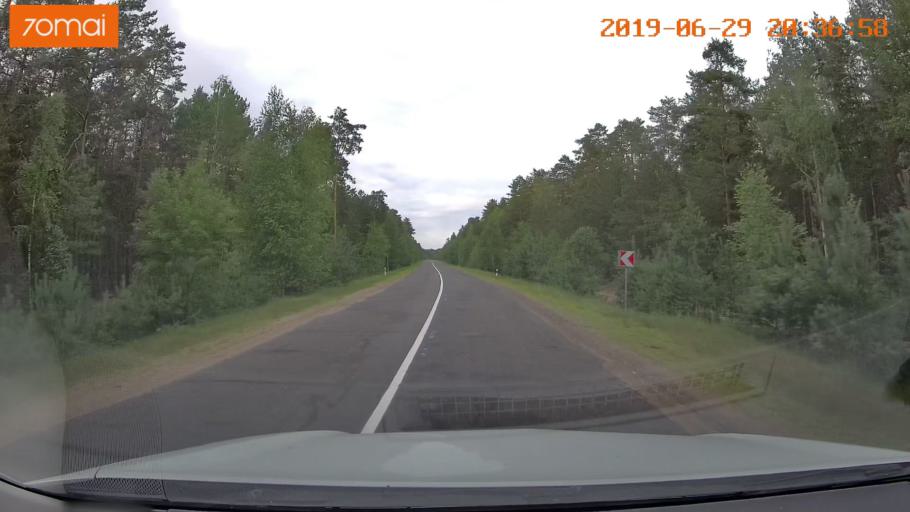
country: BY
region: Brest
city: Hantsavichy
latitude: 52.5322
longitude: 26.3626
